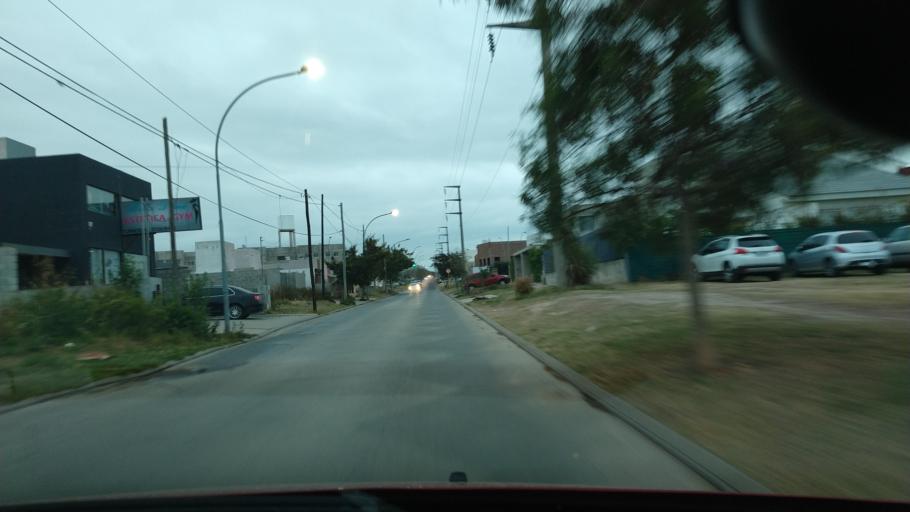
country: AR
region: Cordoba
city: La Calera
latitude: -31.3785
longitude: -64.2684
